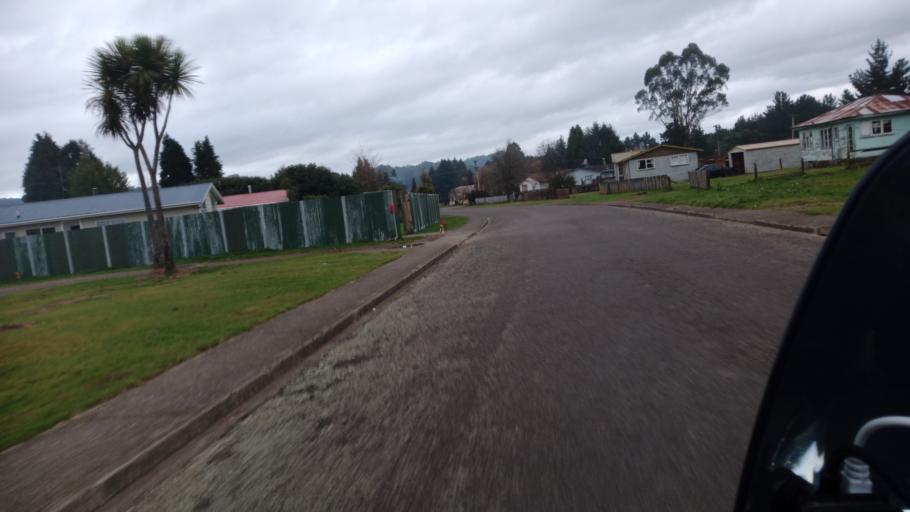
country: NZ
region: Bay of Plenty
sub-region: Whakatane District
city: Murupara
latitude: -38.6438
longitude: 176.7329
